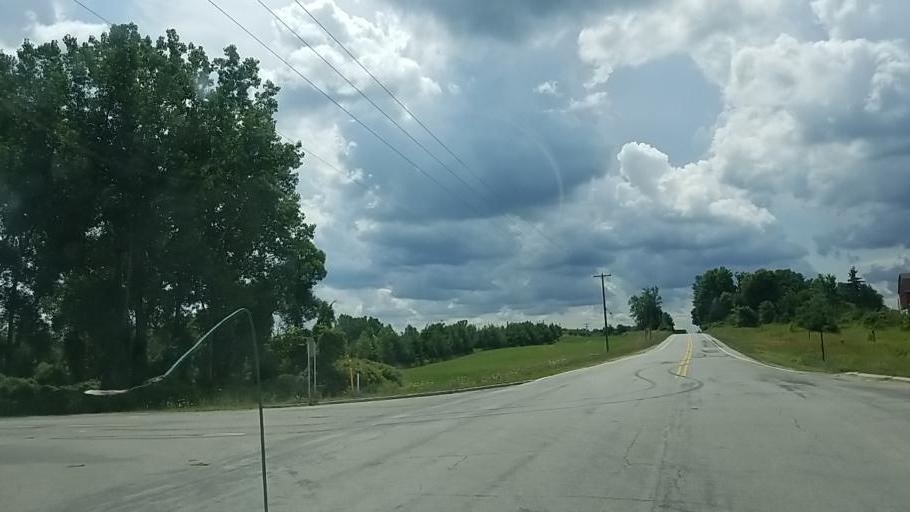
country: US
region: Michigan
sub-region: Kent County
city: Walker
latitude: 43.0742
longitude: -85.7681
